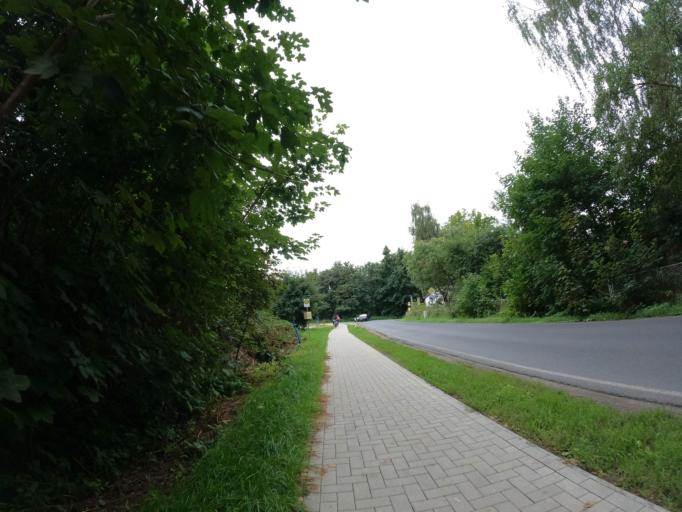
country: DE
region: Mecklenburg-Vorpommern
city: Ostseebad Gohren
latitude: 54.3031
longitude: 13.7020
